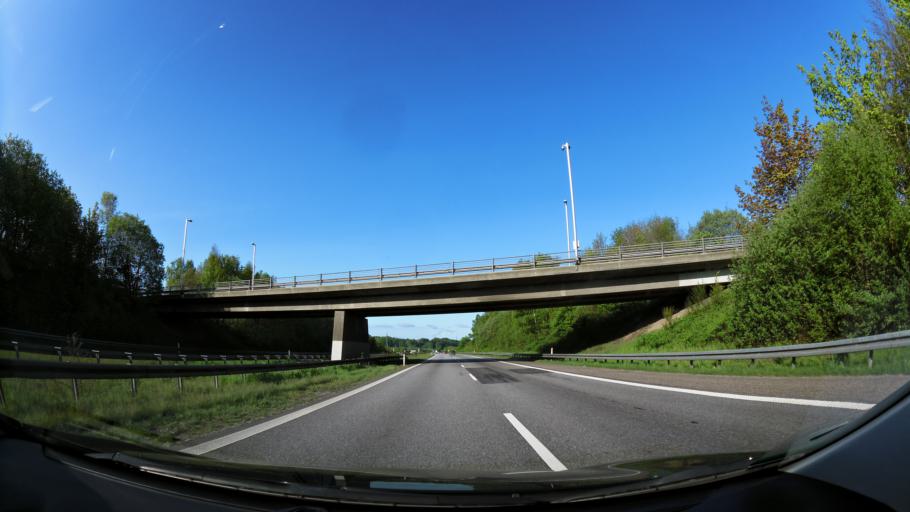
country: DK
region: Central Jutland
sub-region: Skanderborg Kommune
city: Stilling
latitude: 56.0672
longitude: 9.9780
